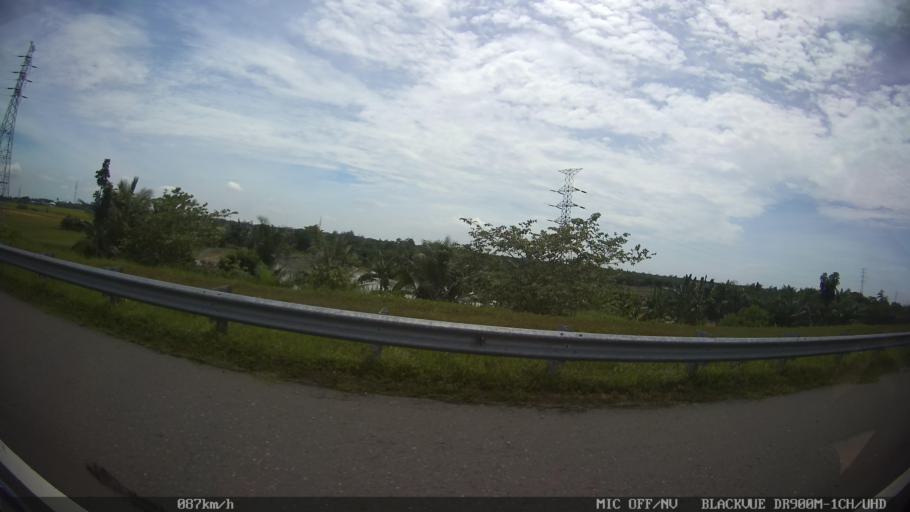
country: ID
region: North Sumatra
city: Percut
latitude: 3.5426
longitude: 98.8548
